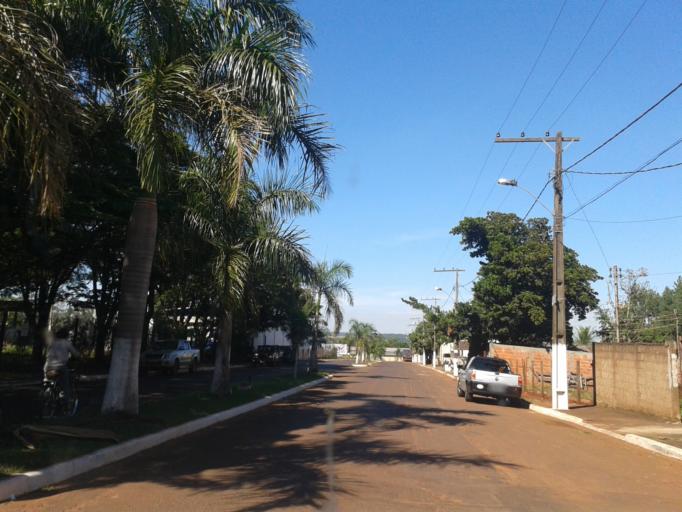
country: BR
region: Minas Gerais
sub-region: Ituiutaba
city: Ituiutaba
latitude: -19.2054
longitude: -49.7847
